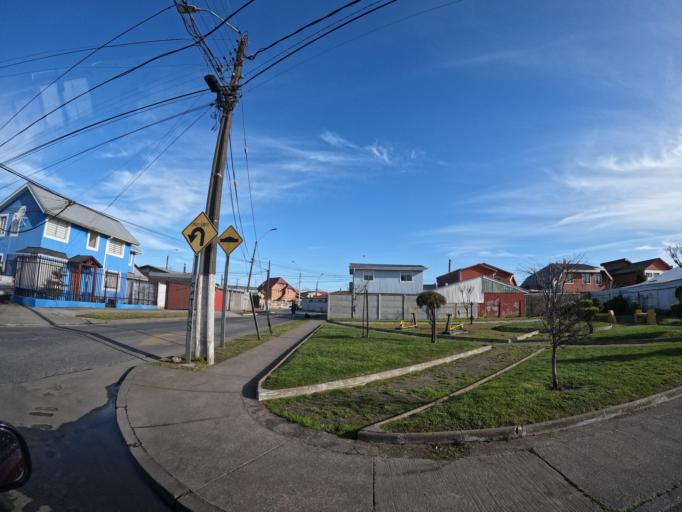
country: CL
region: Biobio
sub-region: Provincia de Concepcion
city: Talcahuano
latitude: -36.7502
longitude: -73.0878
